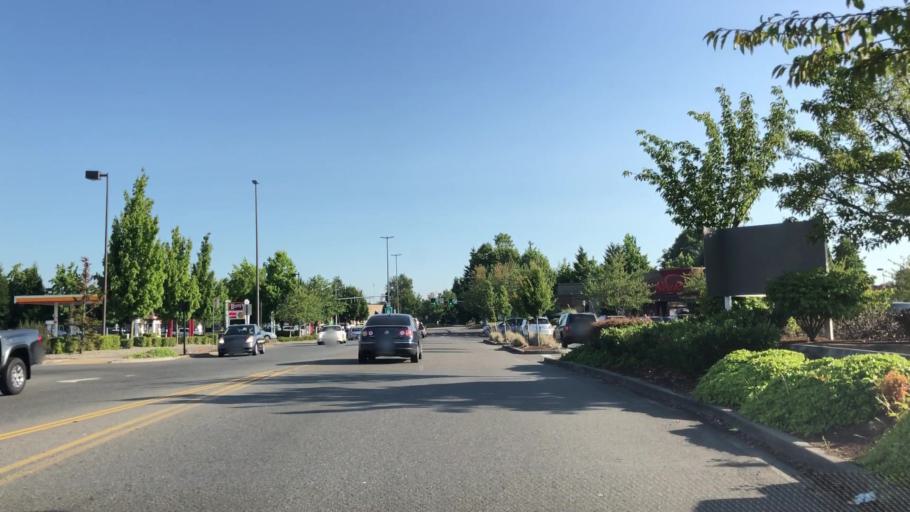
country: US
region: Washington
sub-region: King County
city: Auburn
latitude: 47.2973
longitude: -122.2415
